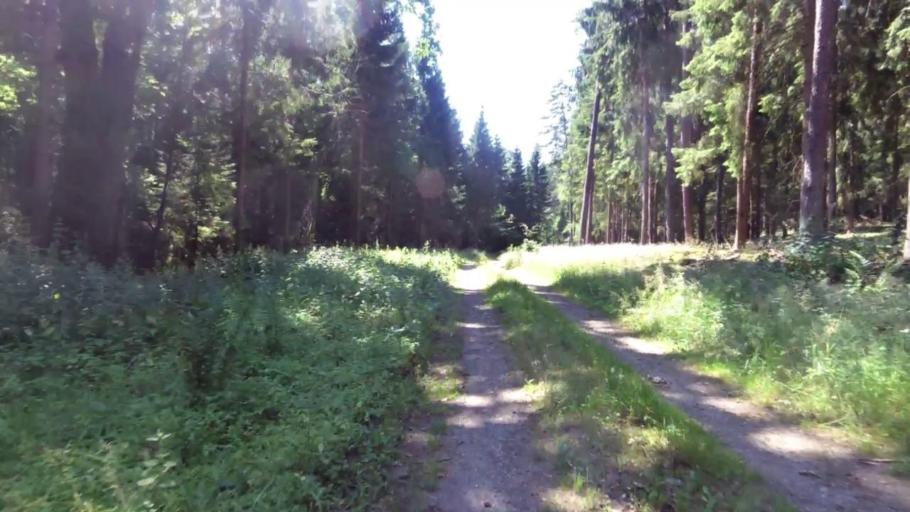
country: PL
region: West Pomeranian Voivodeship
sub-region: Powiat swidwinski
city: Polczyn-Zdroj
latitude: 53.8131
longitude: 16.1264
